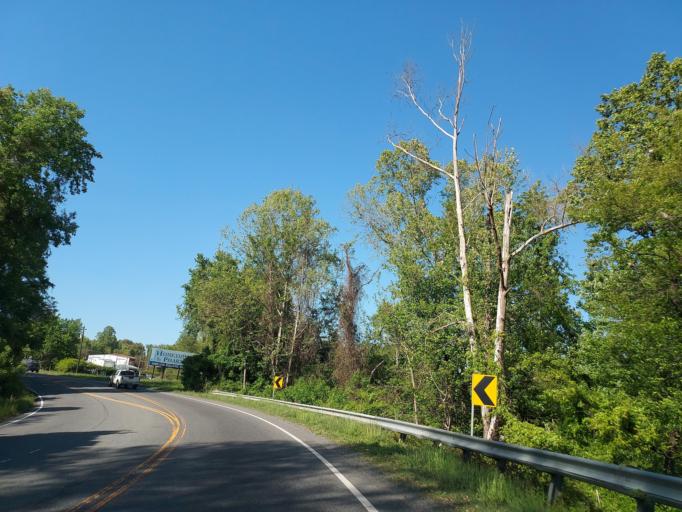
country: US
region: Virginia
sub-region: Amherst County
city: Madison Heights
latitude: 37.4228
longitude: -79.1324
